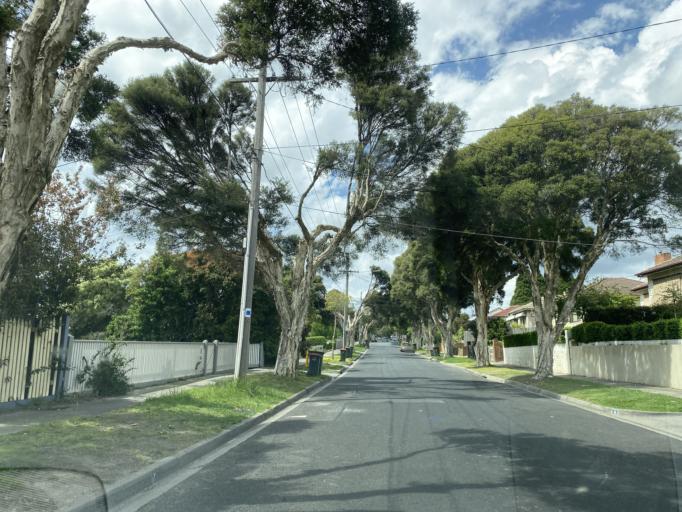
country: AU
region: Victoria
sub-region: Whitehorse
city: Burwood
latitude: -37.8564
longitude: 145.1289
